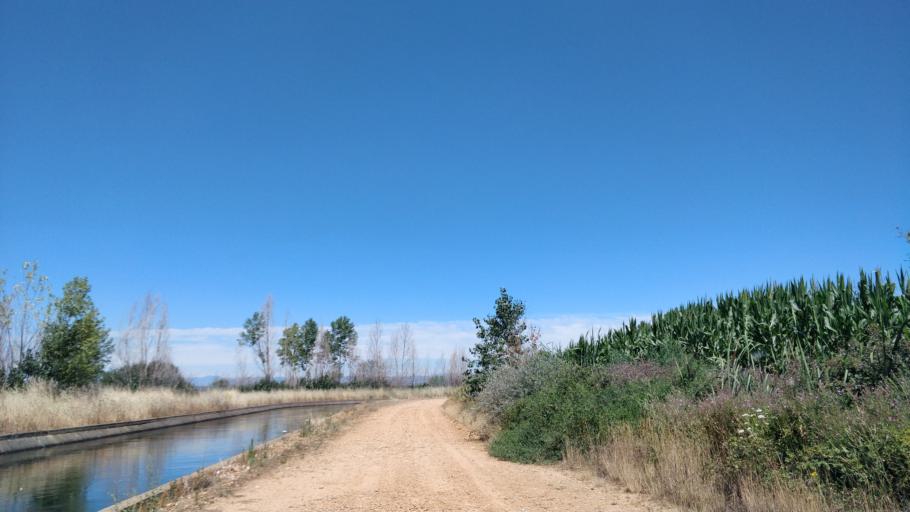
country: ES
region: Castille and Leon
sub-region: Provincia de Leon
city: Bustillo del Paramo
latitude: 42.4743
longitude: -5.8050
